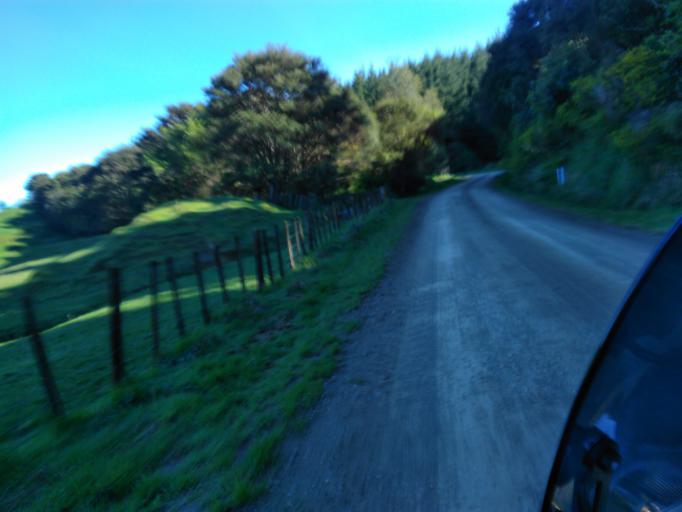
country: NZ
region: Gisborne
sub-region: Gisborne District
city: Gisborne
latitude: -38.3999
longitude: 177.6801
